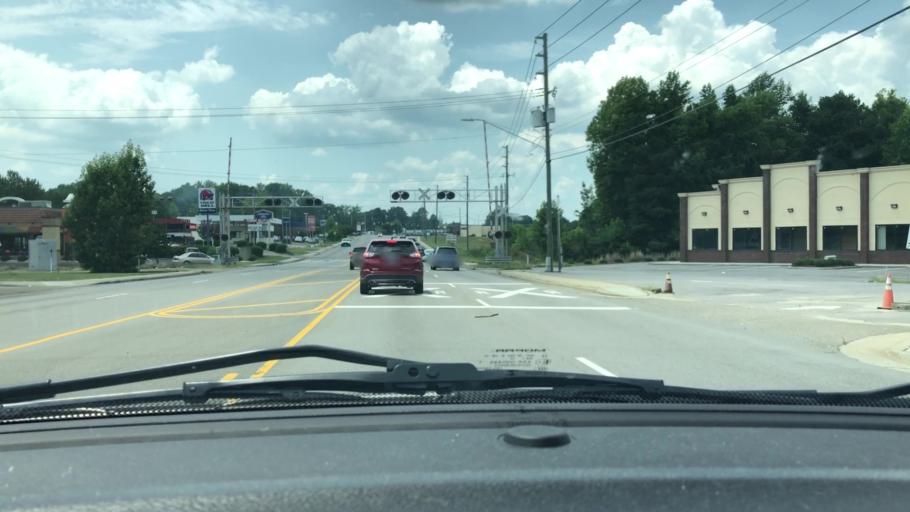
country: US
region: North Carolina
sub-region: Lee County
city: Sanford
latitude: 35.4629
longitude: -79.1550
